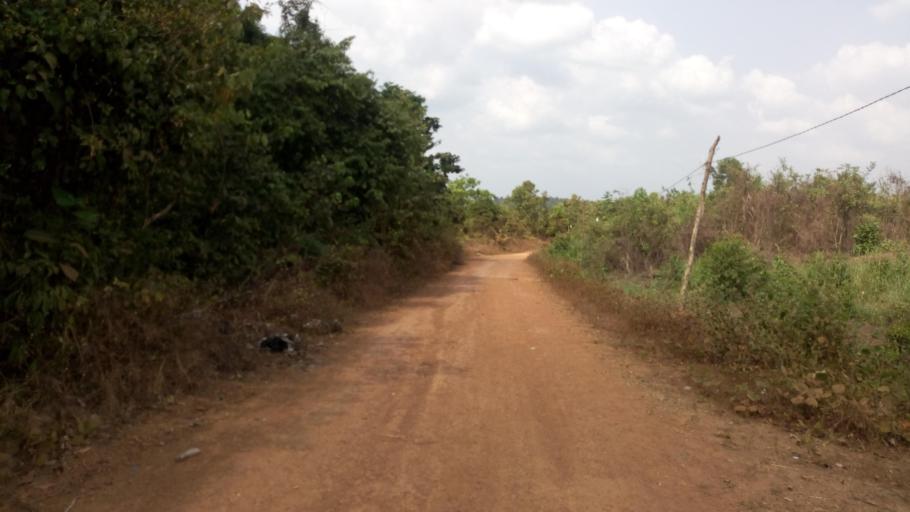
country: SL
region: Southern Province
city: Mogbwemo
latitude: 7.7935
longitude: -12.3074
